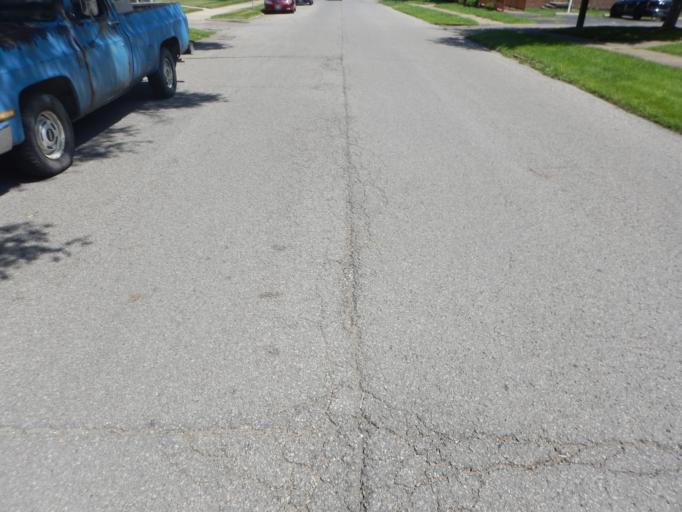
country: US
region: Ohio
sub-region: Muskingum County
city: Zanesville
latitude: 39.9553
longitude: -82.0084
